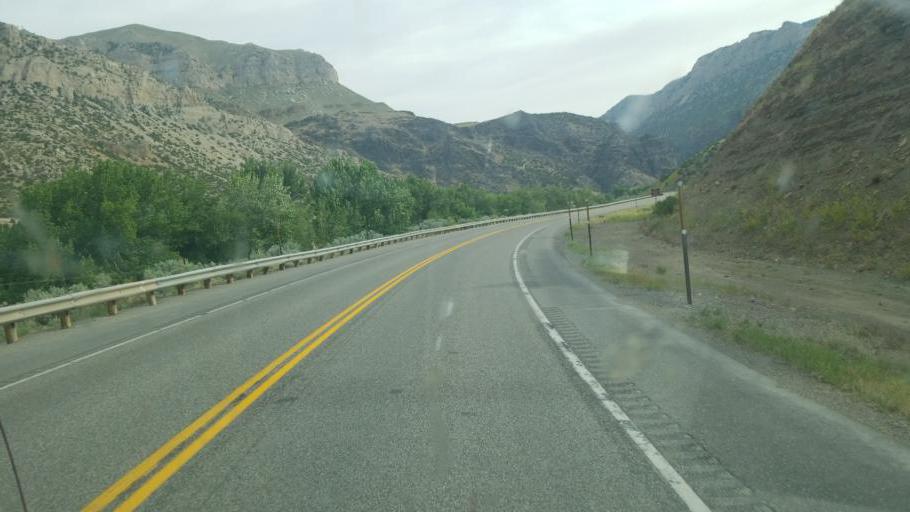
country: US
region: Wyoming
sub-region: Hot Springs County
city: Thermopolis
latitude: 43.4313
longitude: -108.1781
